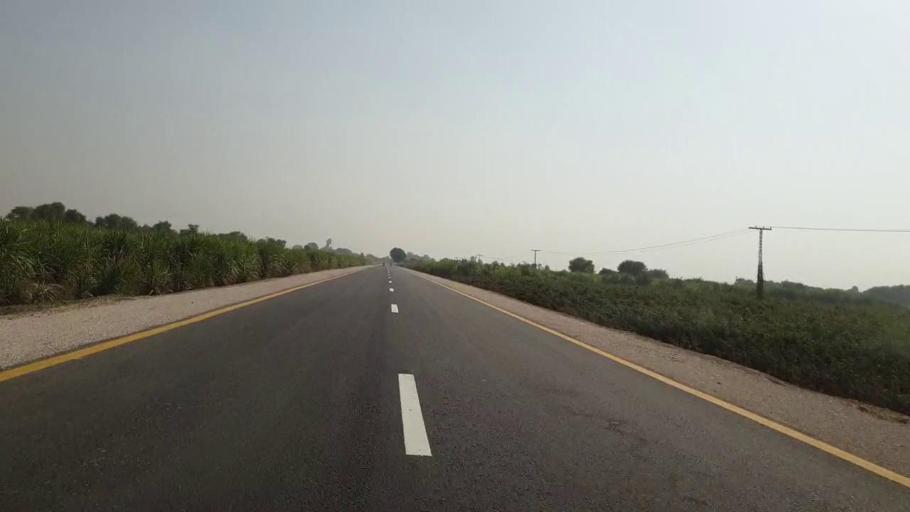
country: PK
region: Sindh
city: Bhan
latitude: 26.6089
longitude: 67.7788
